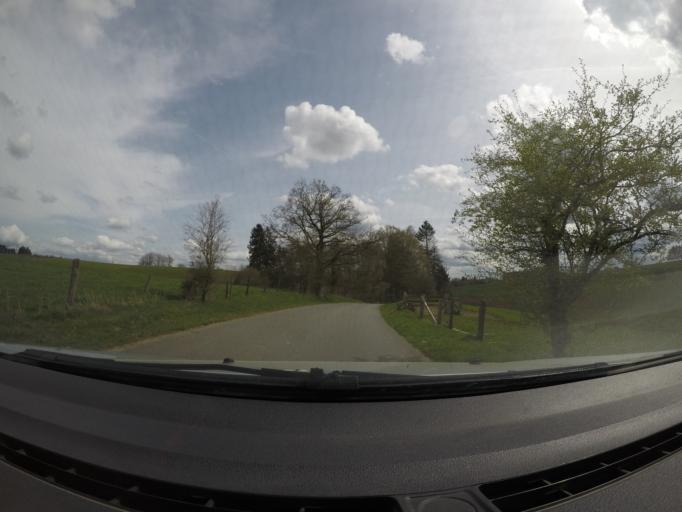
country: BE
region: Wallonia
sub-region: Province du Luxembourg
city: Neufchateau
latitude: 49.8213
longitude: 5.4659
